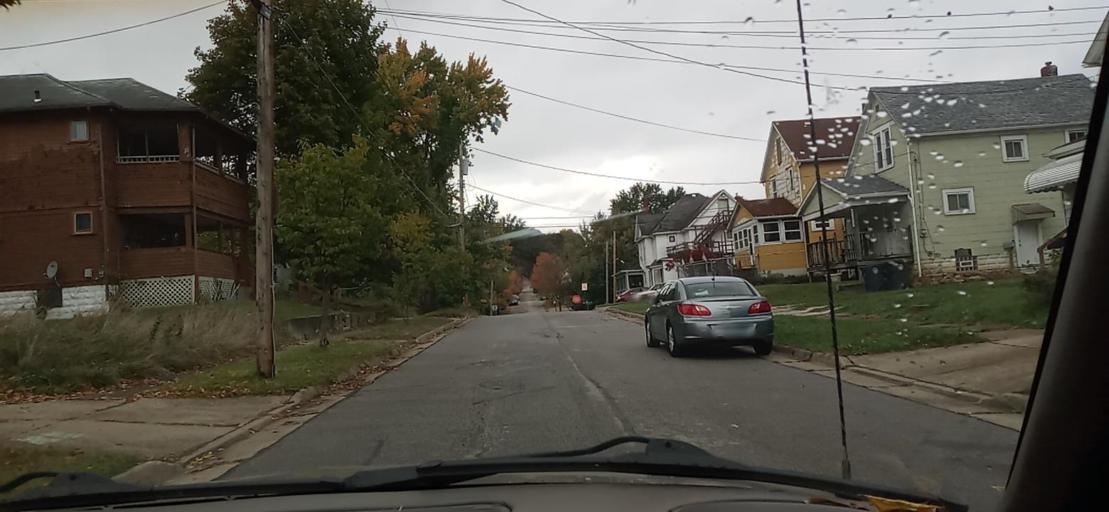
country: US
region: Ohio
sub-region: Summit County
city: Portage Lakes
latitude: 41.0439
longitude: -81.5492
